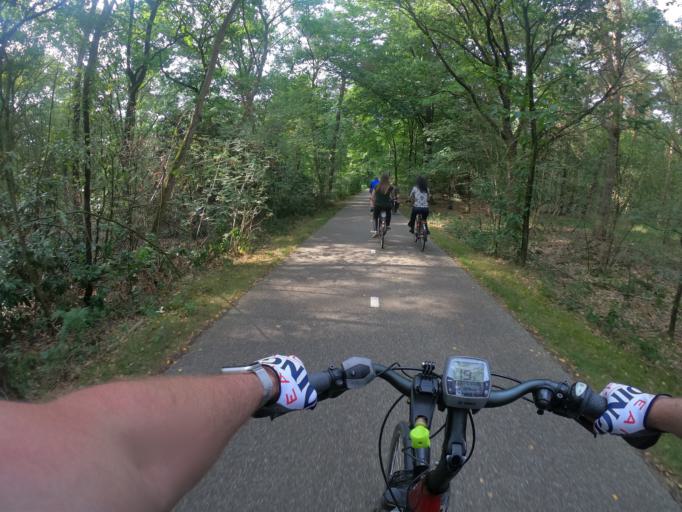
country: NL
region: Gelderland
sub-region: Gemeente Nijmegen
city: Nijmegen
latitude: 51.8053
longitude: 5.8580
